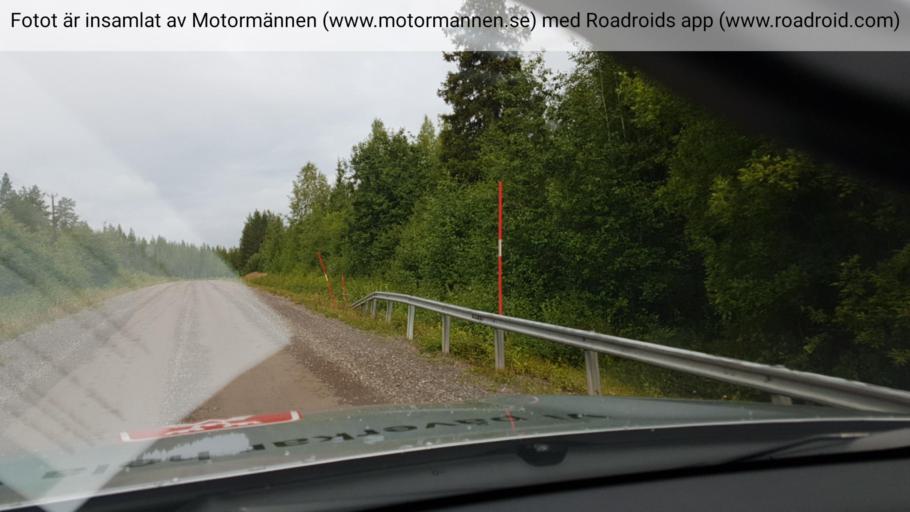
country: SE
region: Norrbotten
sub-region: Alvsbyns Kommun
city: AElvsbyn
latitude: 66.0160
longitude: 21.0424
